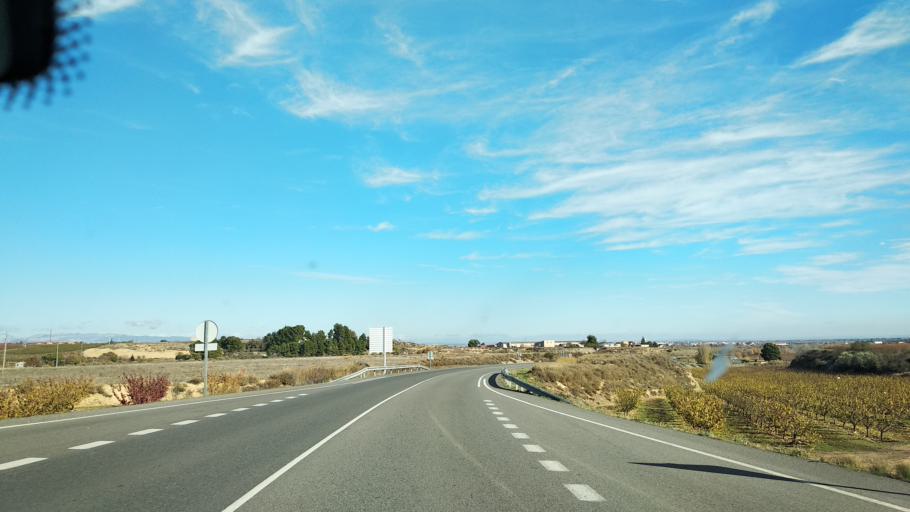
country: ES
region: Catalonia
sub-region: Provincia de Lleida
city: Corbins
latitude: 41.6811
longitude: 0.6815
